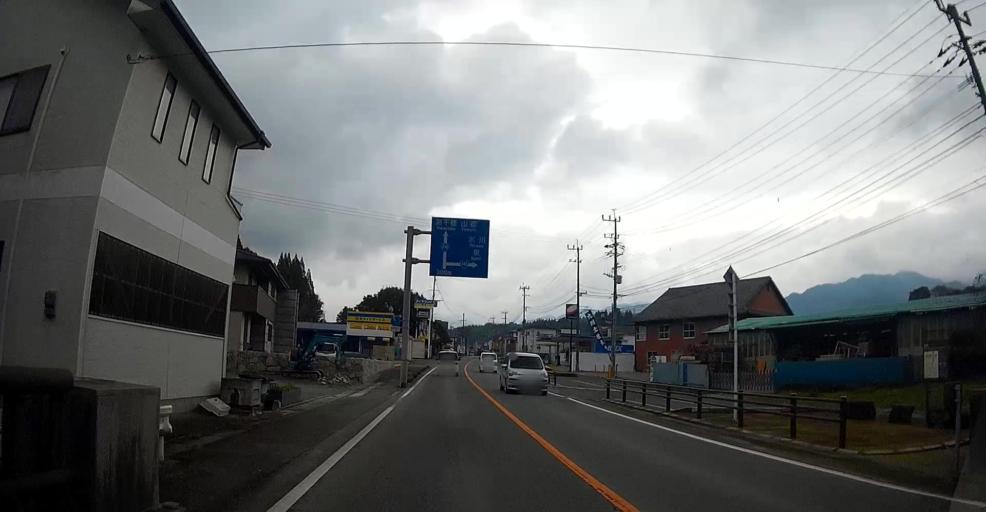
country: JP
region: Kumamoto
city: Matsubase
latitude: 32.6229
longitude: 130.8165
